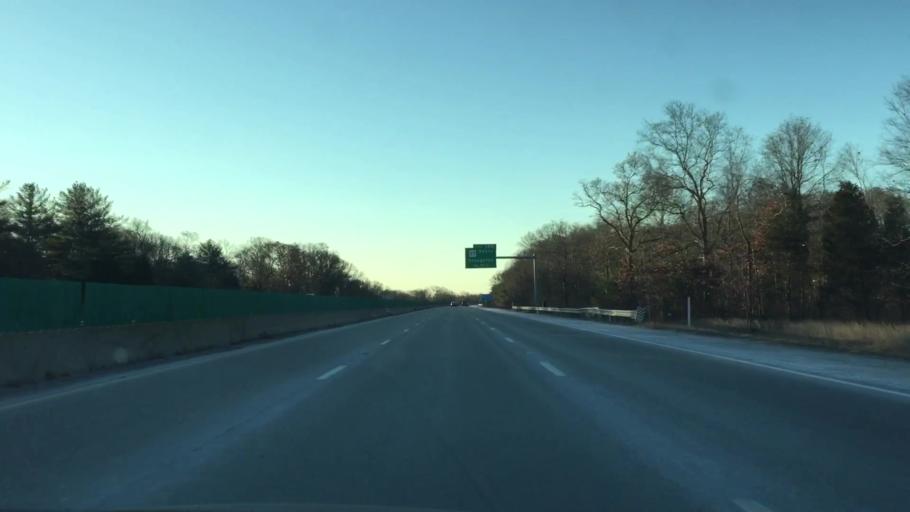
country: US
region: Massachusetts
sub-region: Norfolk County
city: Avon
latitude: 42.1070
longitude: -71.0585
